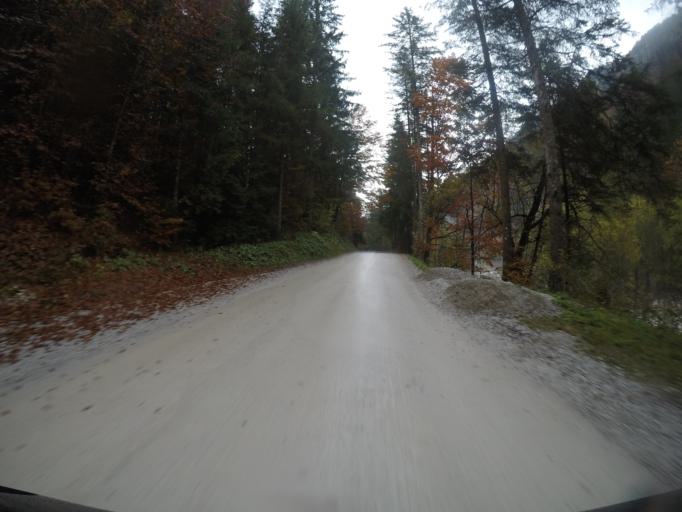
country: SI
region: Kranjska Gora
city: Mojstrana
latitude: 46.4397
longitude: 13.8974
